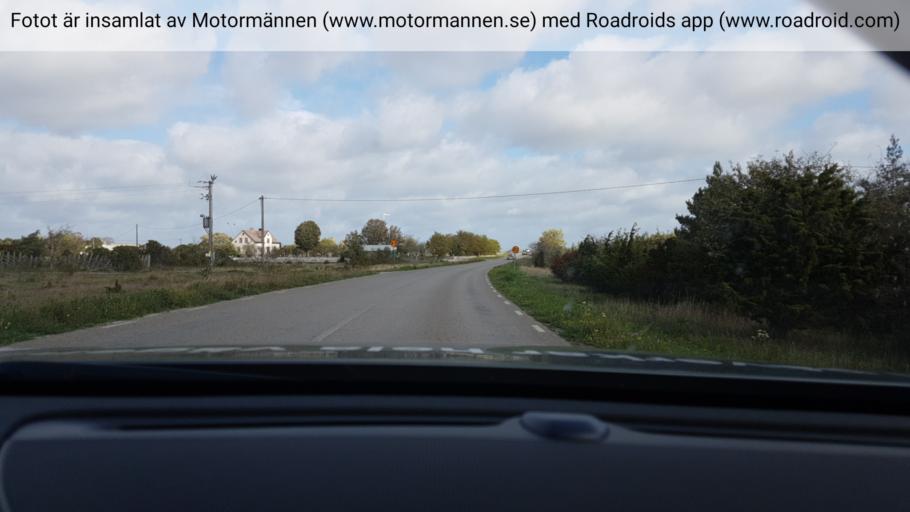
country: SE
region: Gotland
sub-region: Gotland
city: Slite
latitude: 57.9201
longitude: 19.1386
